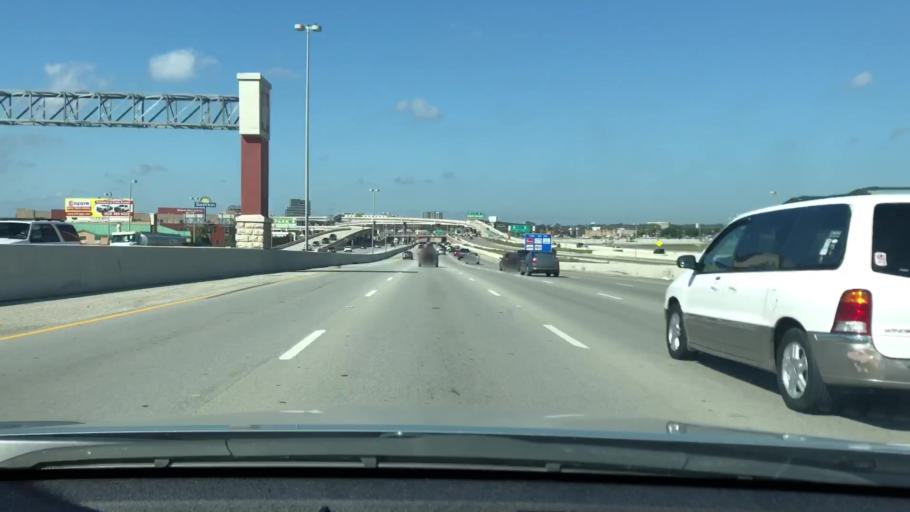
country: US
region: Texas
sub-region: Bexar County
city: Alamo Heights
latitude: 29.5191
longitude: -98.4691
